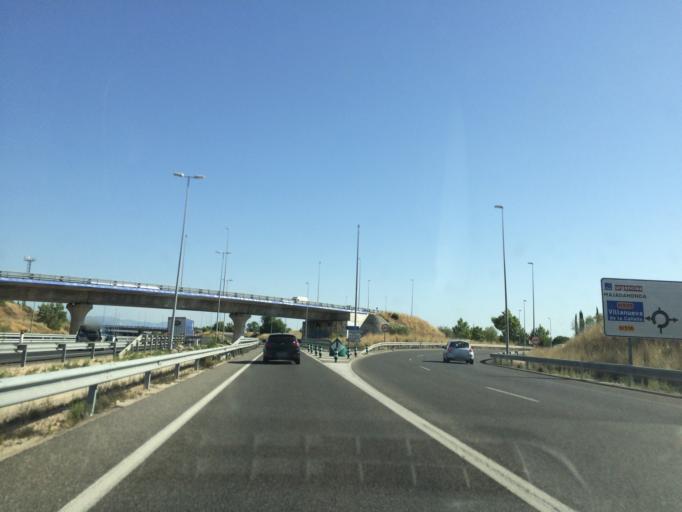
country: ES
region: Madrid
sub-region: Provincia de Madrid
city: Majadahonda
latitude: 40.4500
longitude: -3.8790
